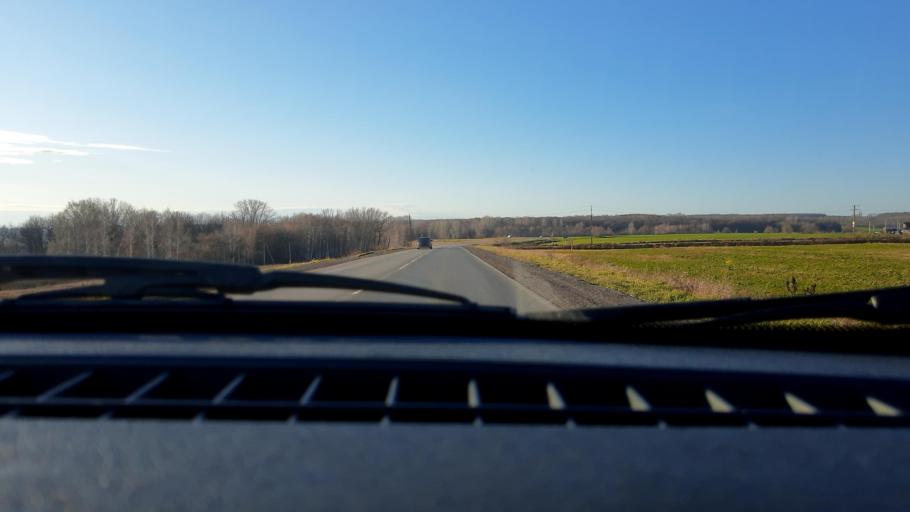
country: RU
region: Bashkortostan
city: Mikhaylovka
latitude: 54.8316
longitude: 55.9469
